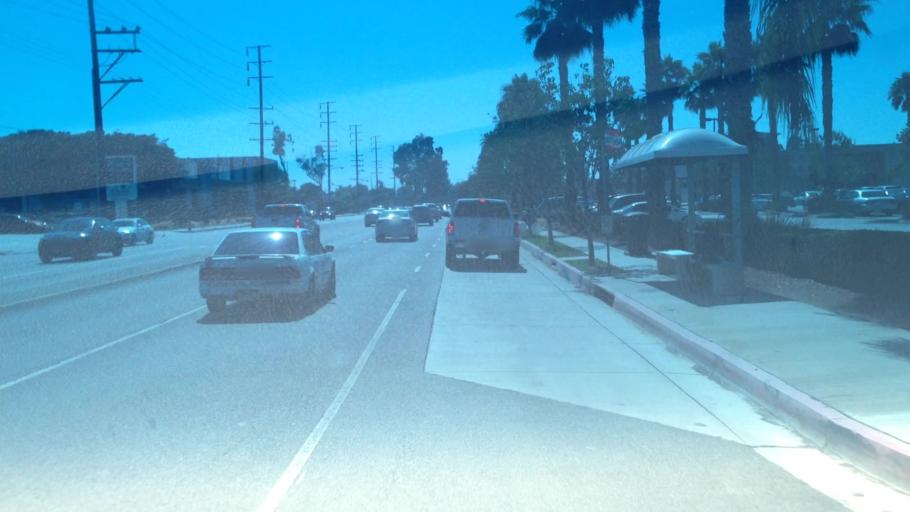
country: US
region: California
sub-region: Orange County
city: Rossmoor
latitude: 33.8106
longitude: -118.1080
